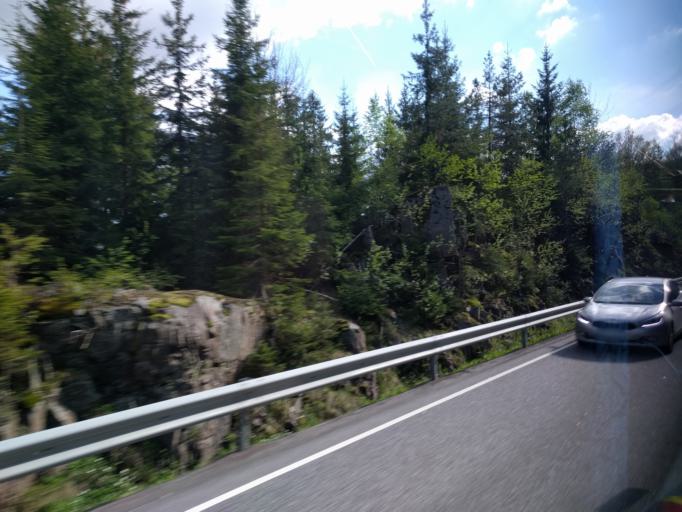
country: NO
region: Vestfold
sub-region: Lardal
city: Svarstad
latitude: 59.3761
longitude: 9.9342
